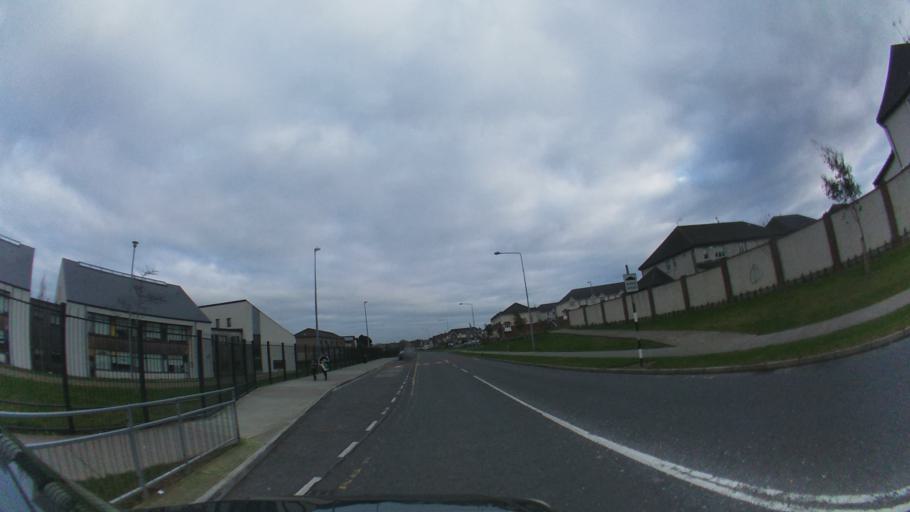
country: IE
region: Leinster
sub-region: Lu
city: Drogheda
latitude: 53.7073
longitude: -6.3388
